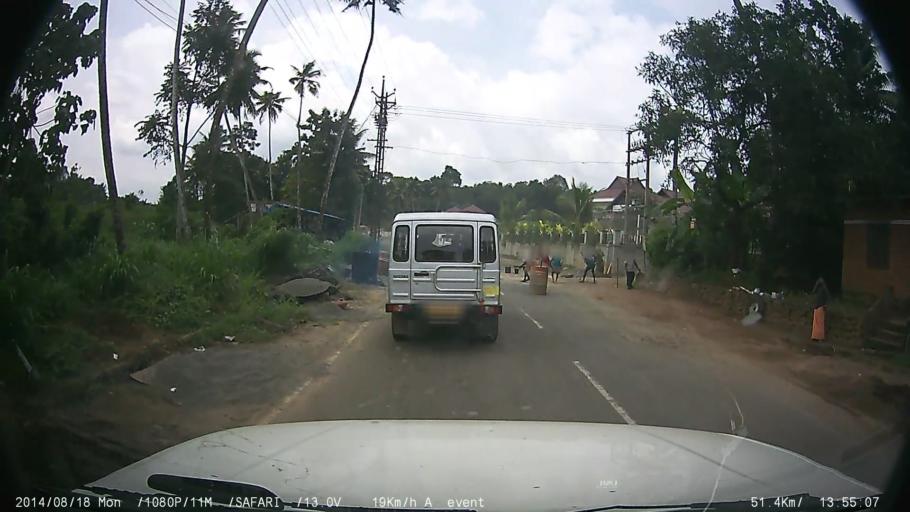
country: IN
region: Kerala
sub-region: Kottayam
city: Palackattumala
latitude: 9.7443
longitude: 76.5610
